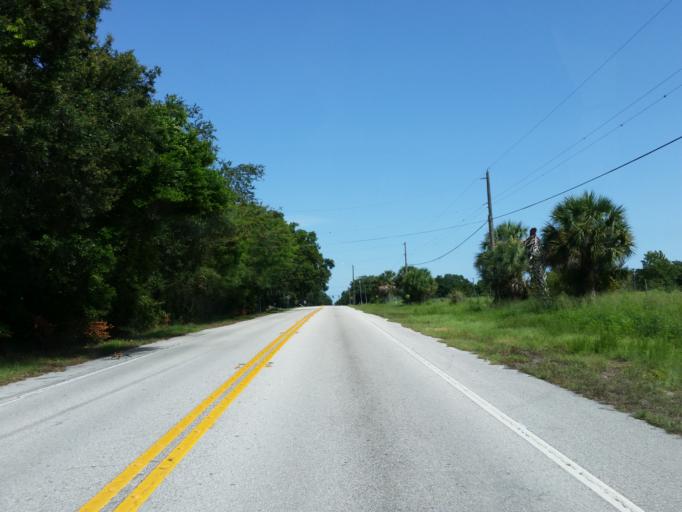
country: US
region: Florida
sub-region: Hillsborough County
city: Bloomingdale
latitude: 27.9054
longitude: -82.2542
